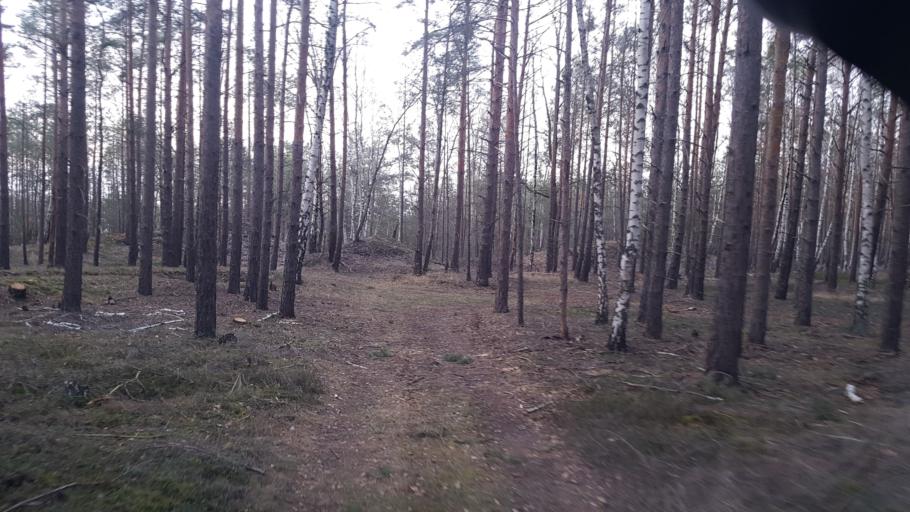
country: DE
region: Brandenburg
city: Schonborn
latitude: 51.5945
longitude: 13.4715
